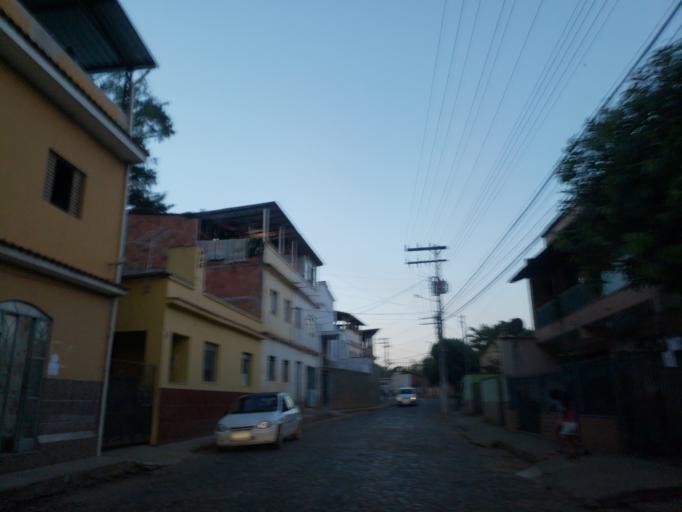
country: BR
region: Minas Gerais
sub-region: Sao Joao Nepomuceno
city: Sao Joao Nepomuceno
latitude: -21.5244
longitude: -43.0149
